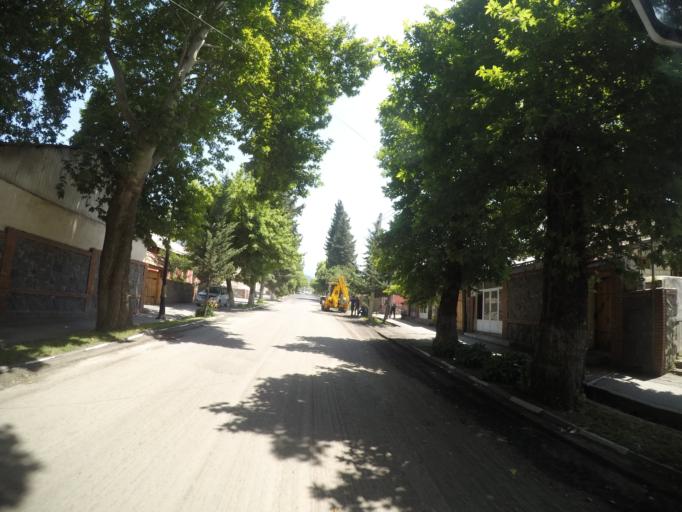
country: AZ
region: Qakh Rayon
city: Qax
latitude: 41.4216
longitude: 46.9277
